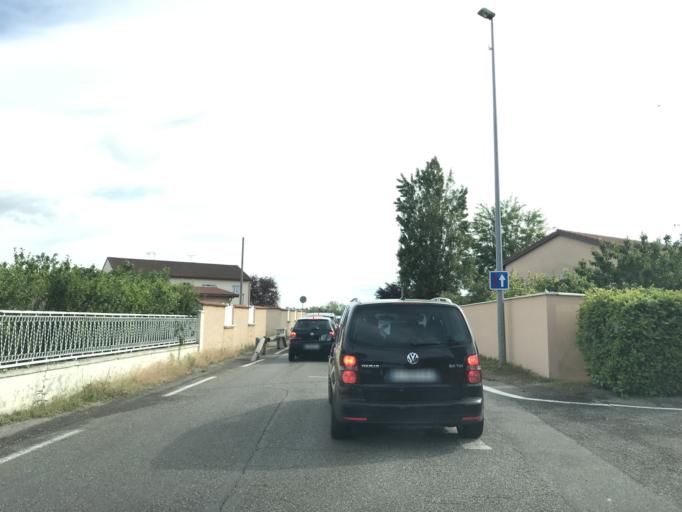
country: FR
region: Rhone-Alpes
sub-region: Departement du Rhone
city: Mions
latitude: 45.6713
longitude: 4.9526
